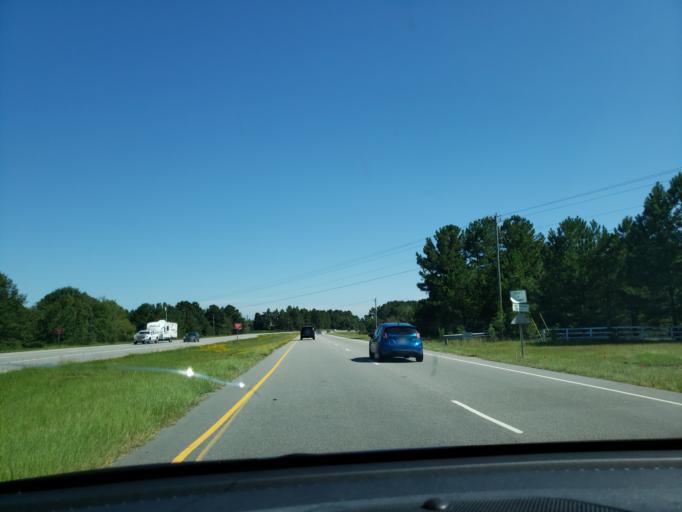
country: US
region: North Carolina
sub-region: Lee County
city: Broadway
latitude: 35.3385
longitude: -79.0990
